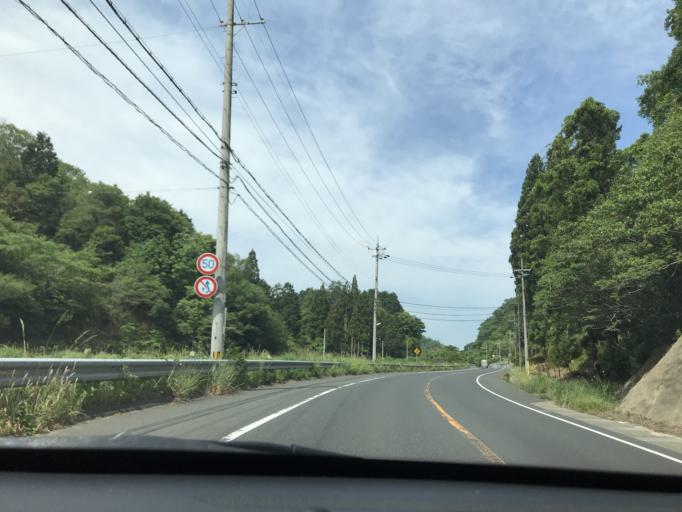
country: JP
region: Kyoto
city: Miyazu
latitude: 35.6589
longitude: 135.0061
